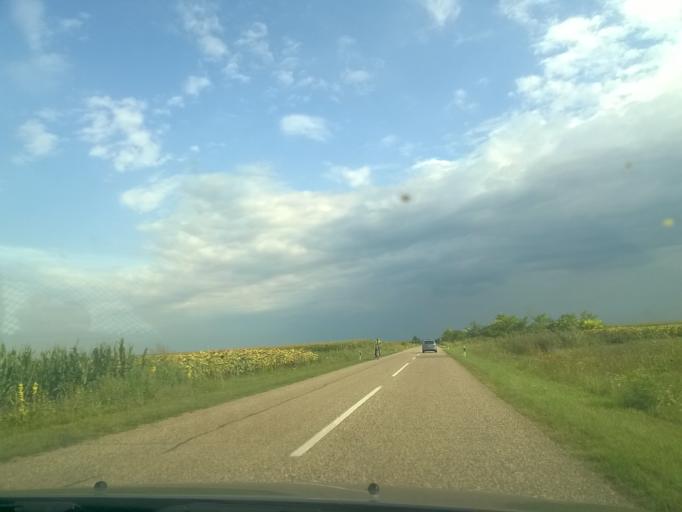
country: RS
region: Autonomna Pokrajina Vojvodina
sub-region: Juznobanatski Okrug
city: Kovacica
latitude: 45.1558
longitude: 20.6170
